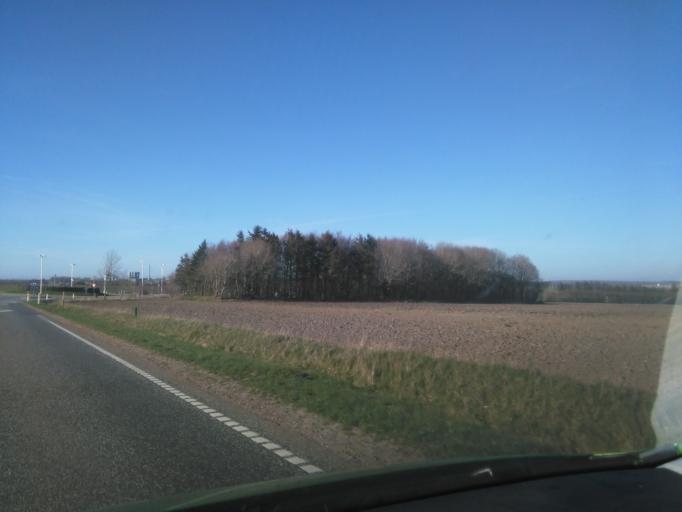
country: DK
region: Central Jutland
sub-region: Ringkobing-Skjern Kommune
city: Videbaek
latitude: 56.0845
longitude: 8.5069
